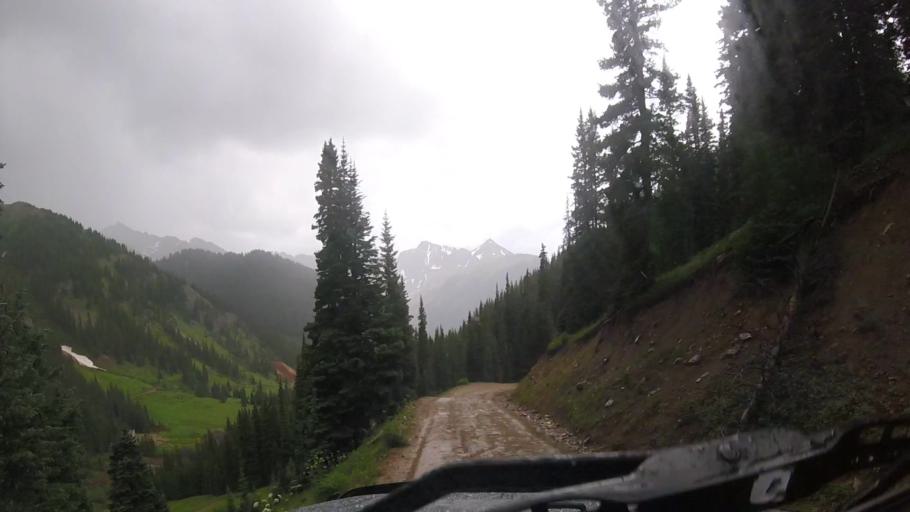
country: US
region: Colorado
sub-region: San Juan County
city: Silverton
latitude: 37.9033
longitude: -107.6472
